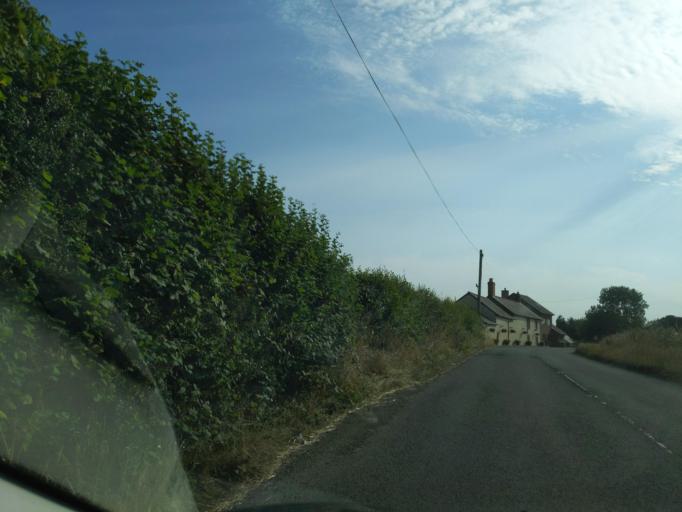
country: GB
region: England
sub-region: Devon
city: Great Torrington
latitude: 50.9650
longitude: -4.0868
